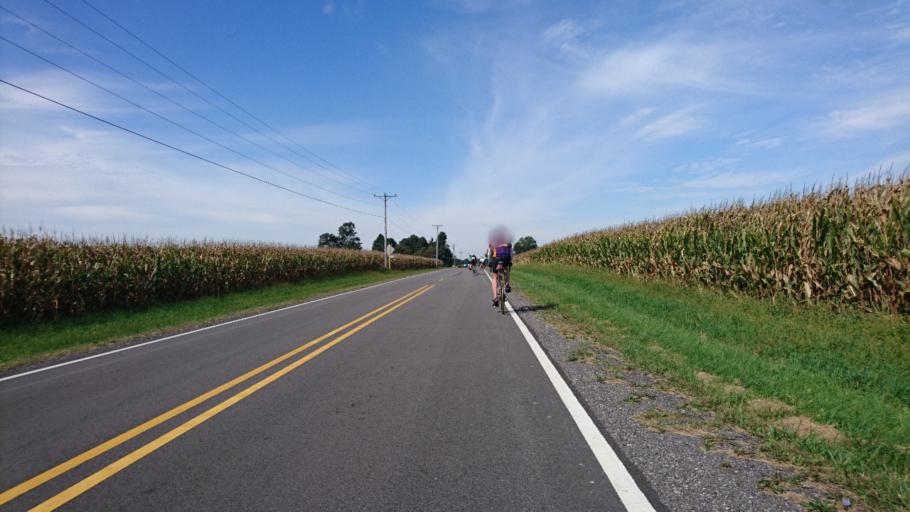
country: US
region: Illinois
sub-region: Will County
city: Elwood
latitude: 41.4083
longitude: -88.0807
